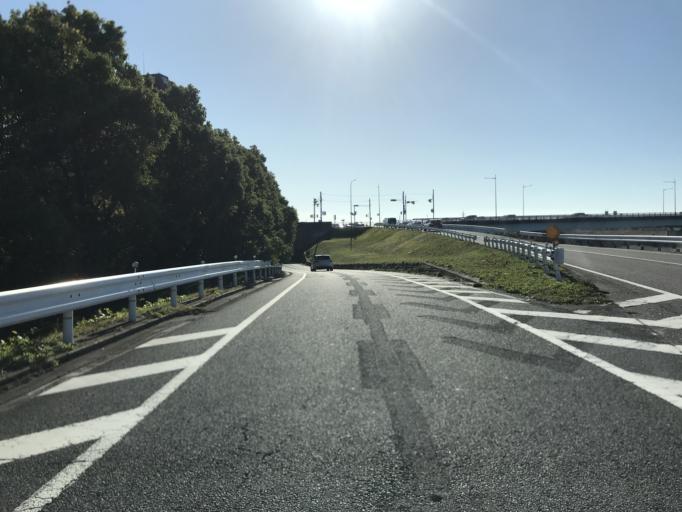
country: JP
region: Aichi
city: Kanie
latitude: 35.1700
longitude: 136.8377
